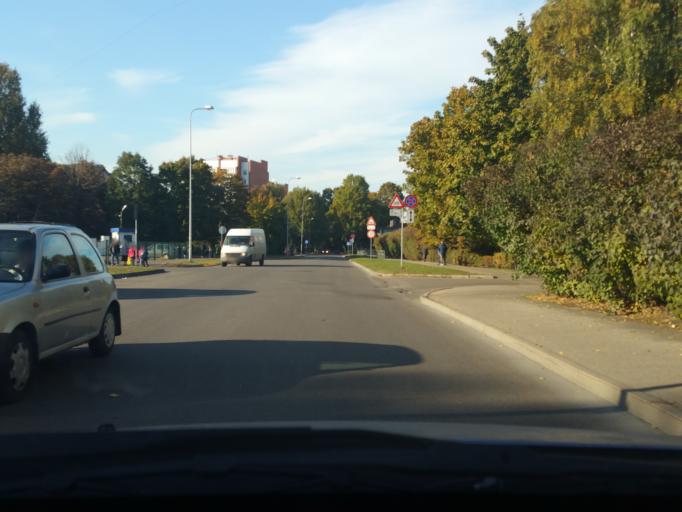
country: LV
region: Riga
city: Jaunciems
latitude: 56.9598
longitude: 24.1857
